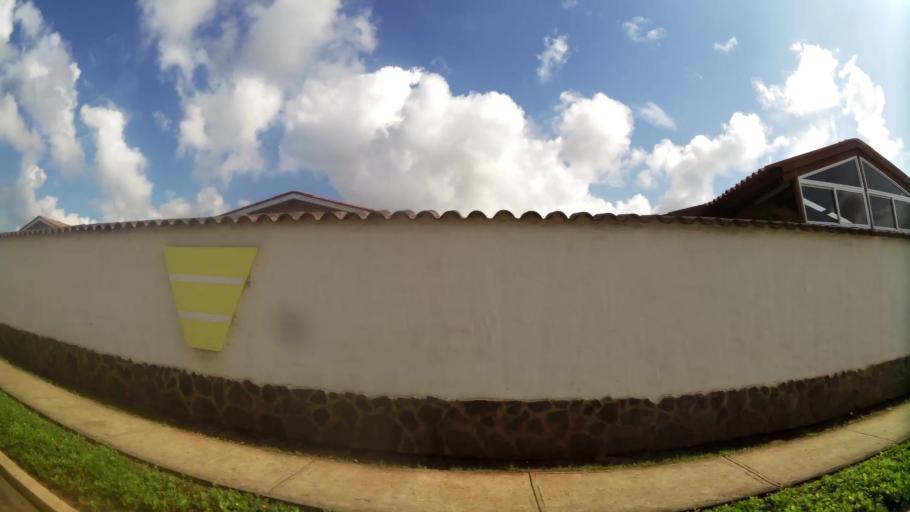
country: PA
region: Panama
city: Nuevo Arraijan
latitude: 8.9021
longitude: -79.7439
